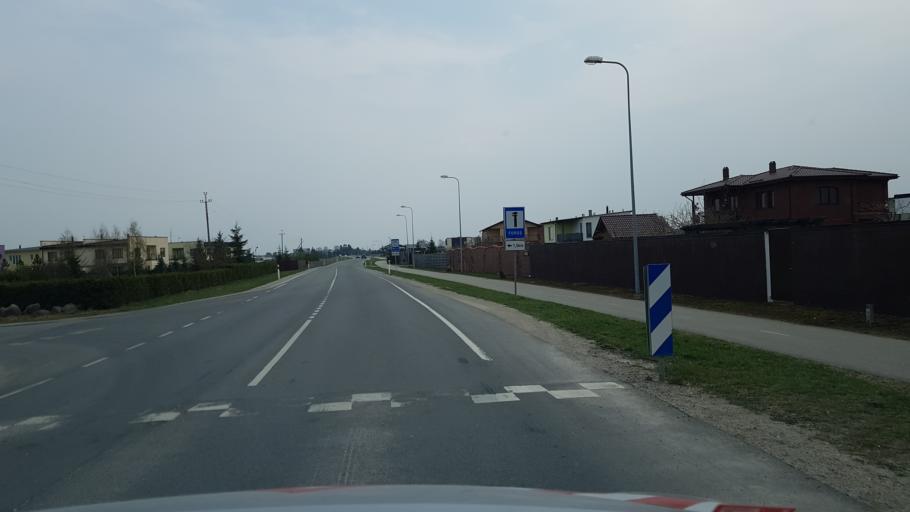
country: EE
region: Harju
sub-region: Tallinna linn
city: Tallinn
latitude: 59.3897
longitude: 24.8042
